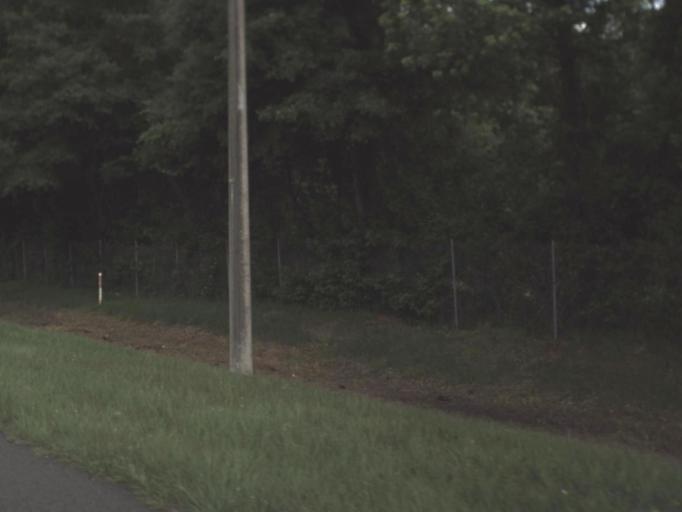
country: US
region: Florida
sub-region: Duval County
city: Jacksonville
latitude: 30.3571
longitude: -81.7080
